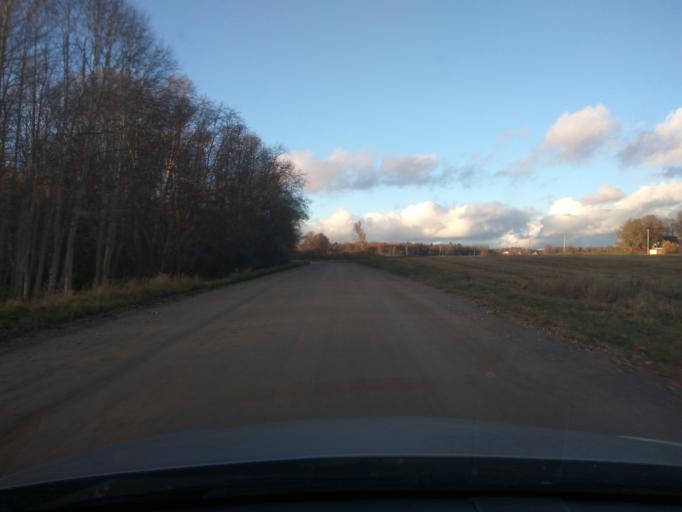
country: LV
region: Aizpute
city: Aizpute
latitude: 56.8182
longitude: 21.7767
